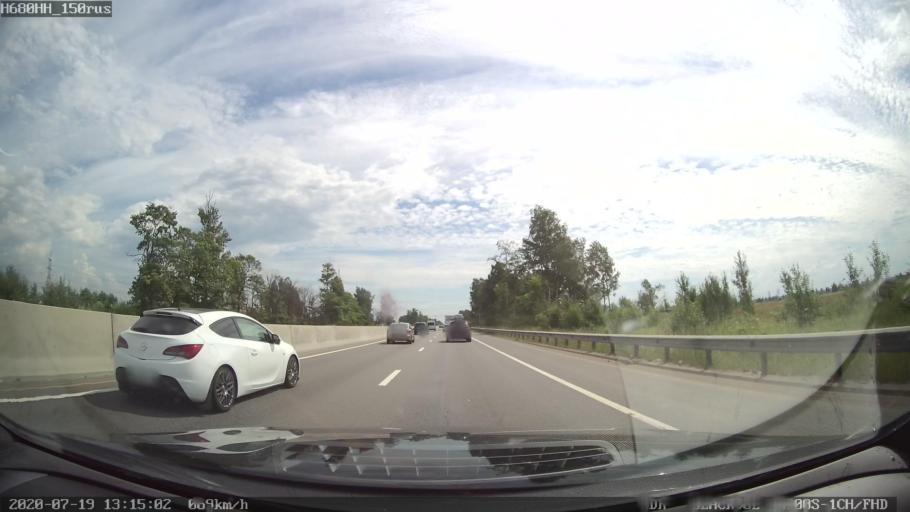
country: RU
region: St.-Petersburg
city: Kolpino
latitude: 59.7286
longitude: 30.5338
